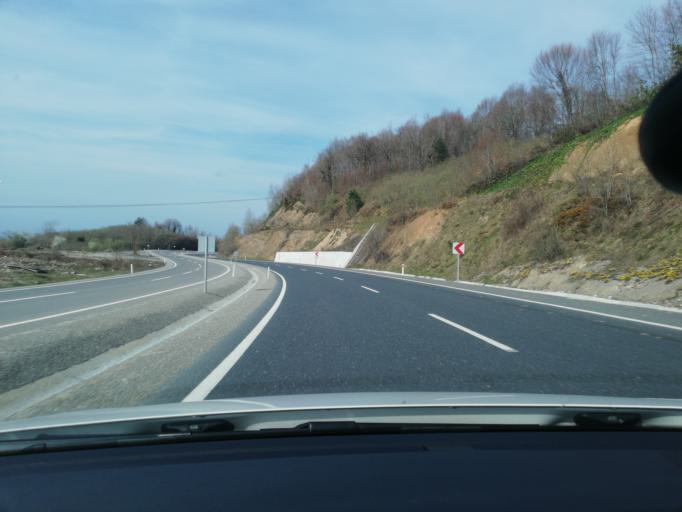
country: TR
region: Zonguldak
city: Kozlu
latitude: 41.3384
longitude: 31.6291
